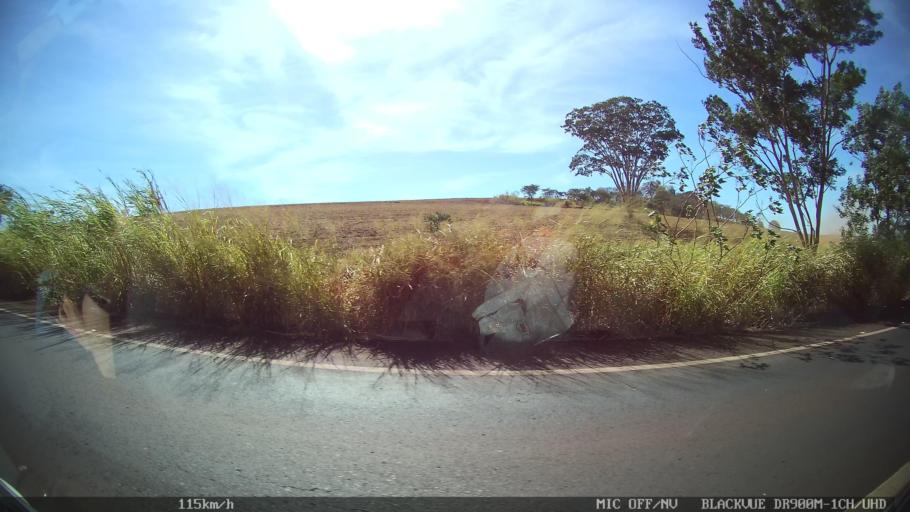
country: BR
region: Sao Paulo
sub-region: Sao Joaquim Da Barra
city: Sao Joaquim da Barra
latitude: -20.5612
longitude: -47.6886
